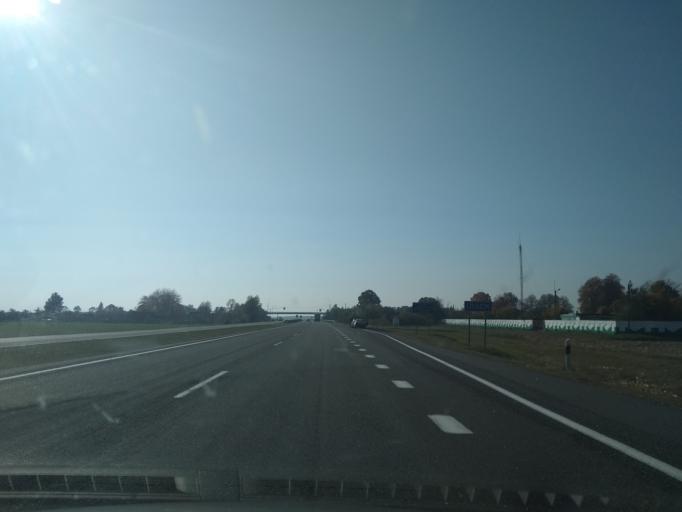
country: BY
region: Brest
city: Antopal'
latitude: 52.3352
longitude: 24.6397
